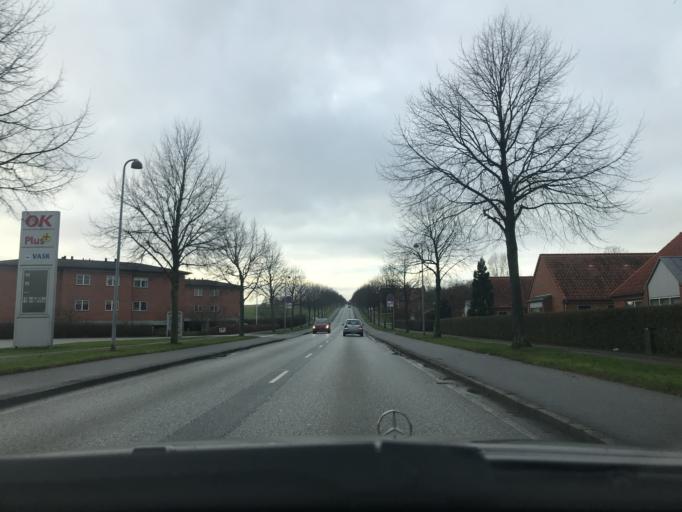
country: DK
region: South Denmark
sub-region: Sonderborg Kommune
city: Sonderborg
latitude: 54.9103
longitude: 9.7726
